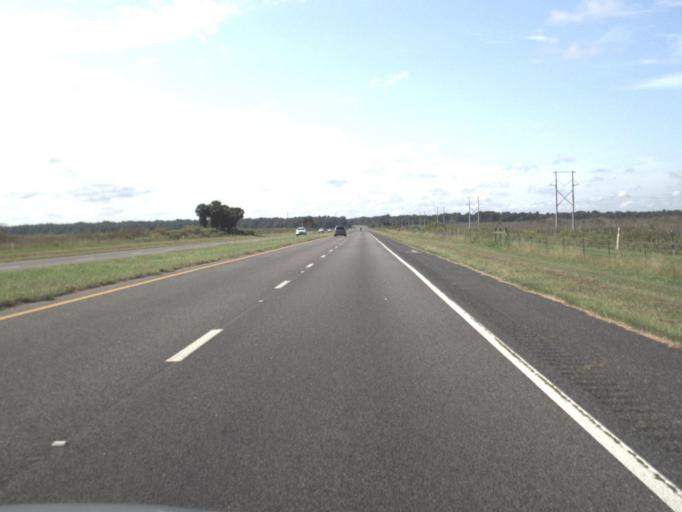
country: US
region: Florida
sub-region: Alachua County
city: Gainesville
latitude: 29.5804
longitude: -82.3370
